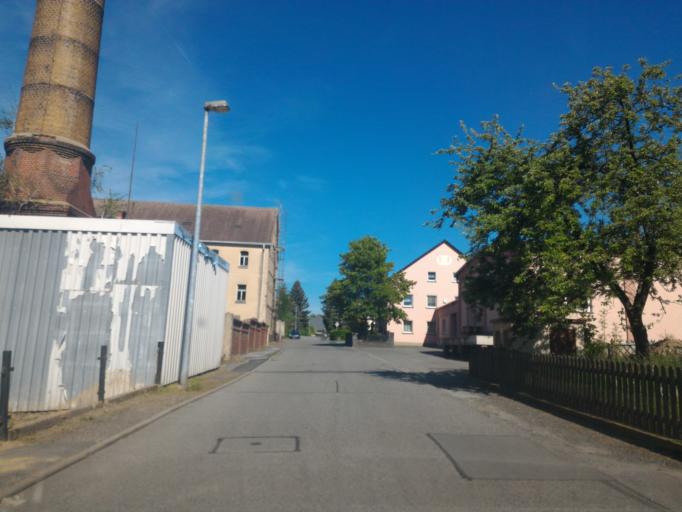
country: DE
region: Saxony
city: Leutersdorf
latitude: 50.9697
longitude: 14.6447
